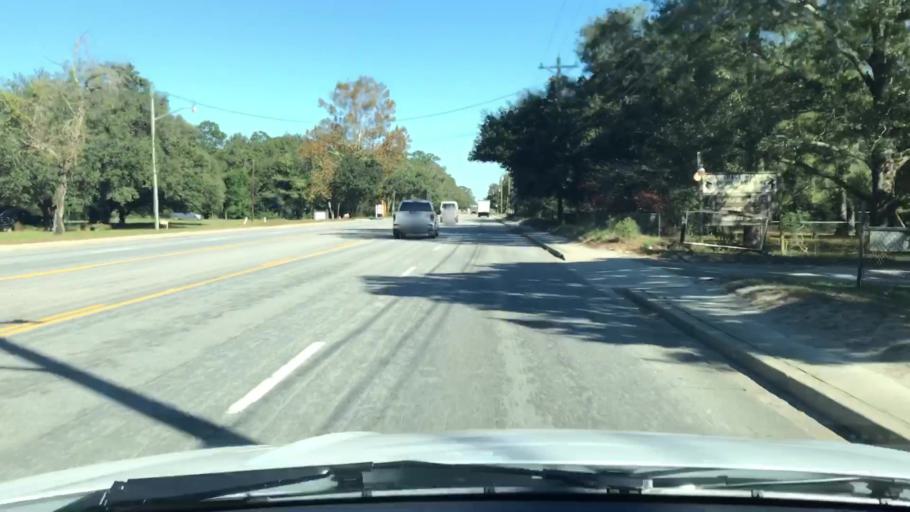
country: US
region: South Carolina
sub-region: Charleston County
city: Ravenel
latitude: 32.7788
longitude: -80.2342
